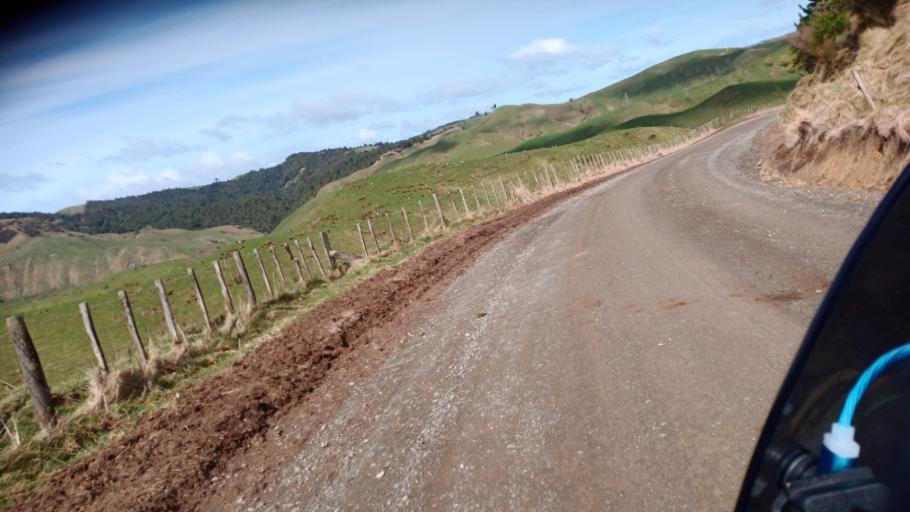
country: NZ
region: Hawke's Bay
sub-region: Wairoa District
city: Wairoa
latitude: -38.7375
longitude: 177.2958
